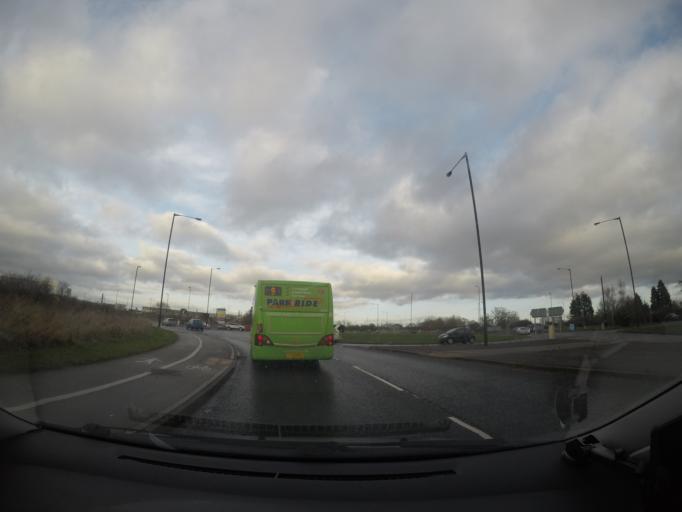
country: GB
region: England
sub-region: City of York
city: Huntington
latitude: 53.9799
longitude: -1.0490
